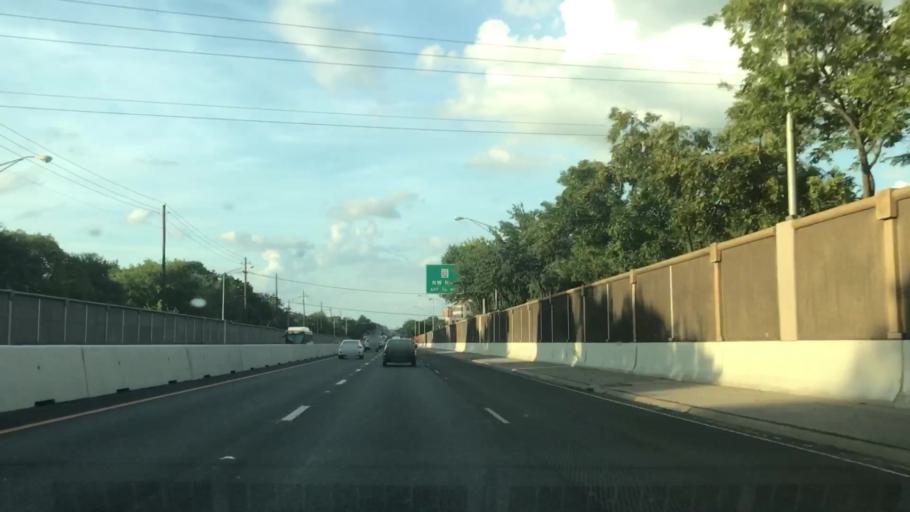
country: US
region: Texas
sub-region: Dallas County
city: University Park
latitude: 32.8573
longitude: -96.8124
